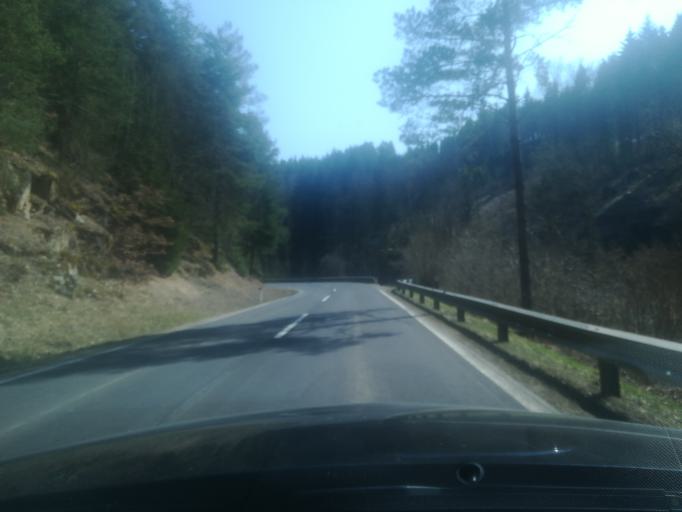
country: AT
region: Upper Austria
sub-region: Politischer Bezirk Freistadt
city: Freistadt
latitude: 48.4382
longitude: 14.5574
